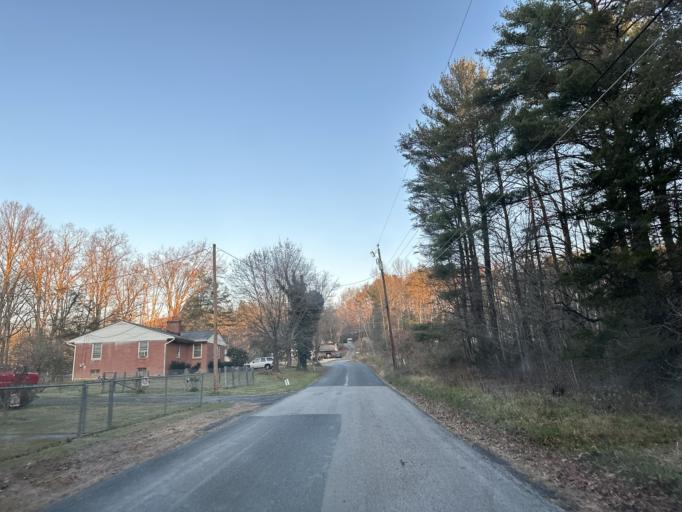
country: US
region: Virginia
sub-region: Rockbridge County
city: East Lexington
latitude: 38.0800
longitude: -79.3895
